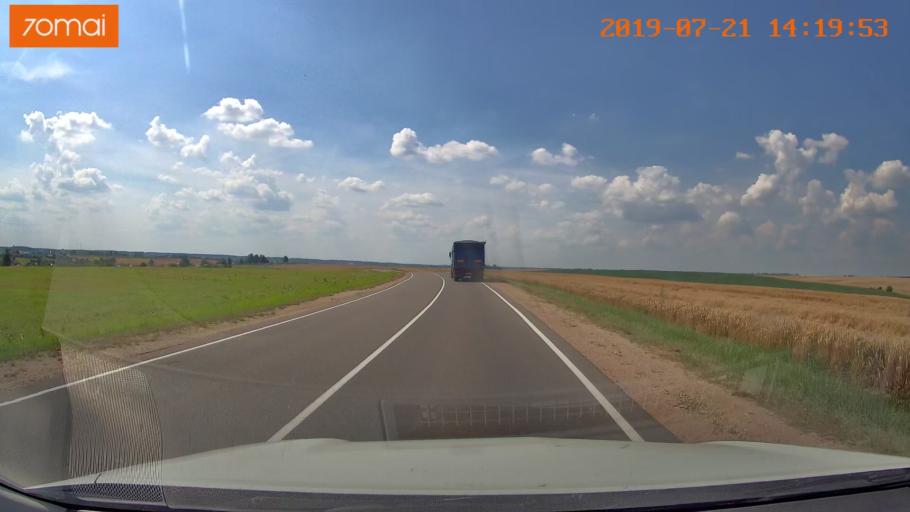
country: BY
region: Grodnenskaya
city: Karelichy
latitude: 53.5866
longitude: 26.1640
